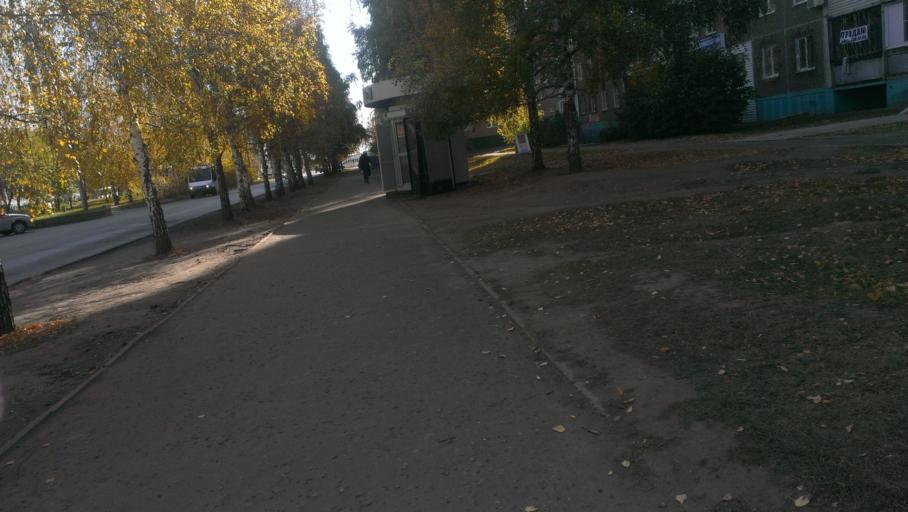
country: RU
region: Altai Krai
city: Novosilikatnyy
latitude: 53.3322
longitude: 83.6761
